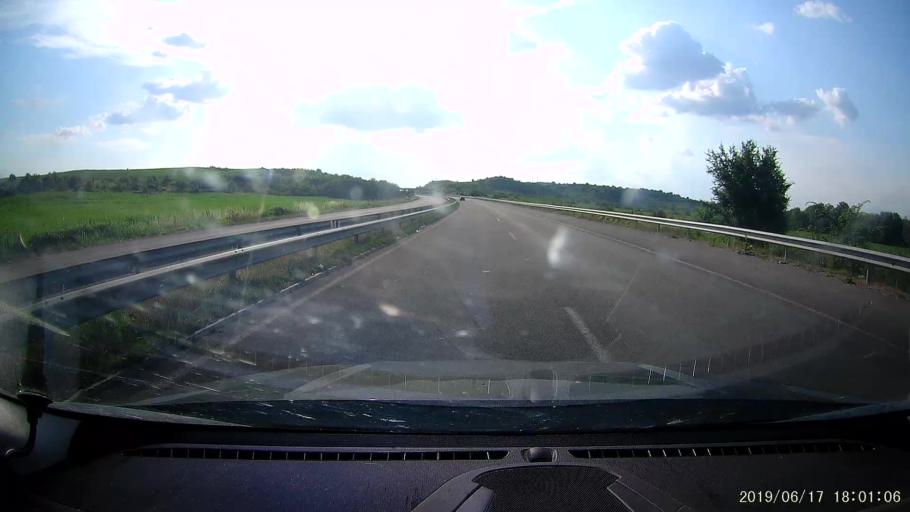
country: BG
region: Khaskovo
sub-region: Obshtina Svilengrad
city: Svilengrad
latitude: 41.7440
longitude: 26.2641
